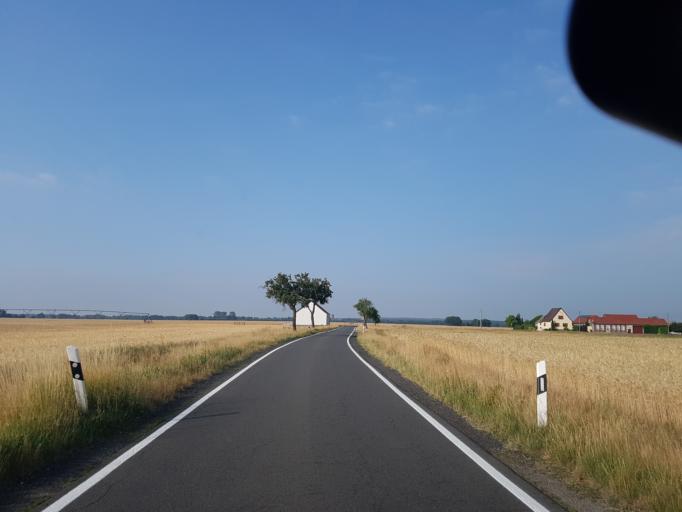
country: DE
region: Saxony-Anhalt
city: Jessen
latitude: 51.8515
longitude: 13.0381
